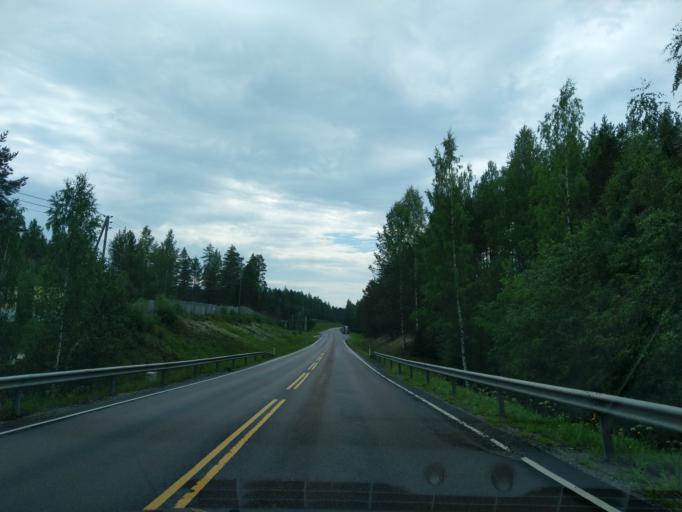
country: FI
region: Southern Savonia
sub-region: Savonlinna
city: Punkaharju
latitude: 61.6885
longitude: 29.4209
